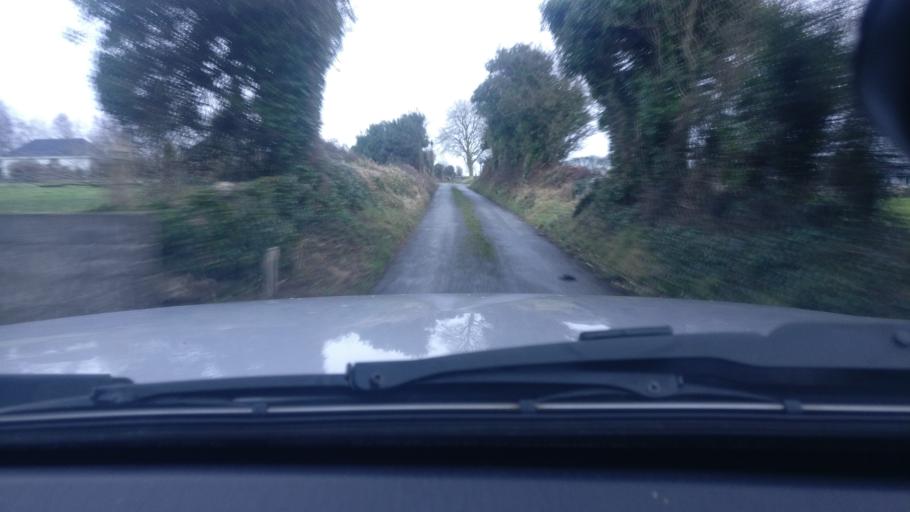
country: IE
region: Connaught
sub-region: County Galway
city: Loughrea
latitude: 53.1863
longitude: -8.6110
